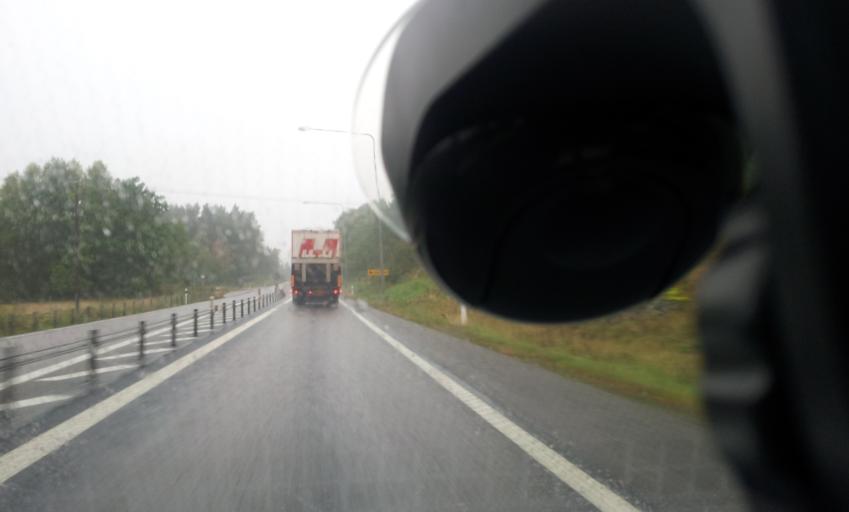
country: SE
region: OEstergoetland
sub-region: Soderkopings Kommun
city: Soederkoeping
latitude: 58.4392
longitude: 16.3743
